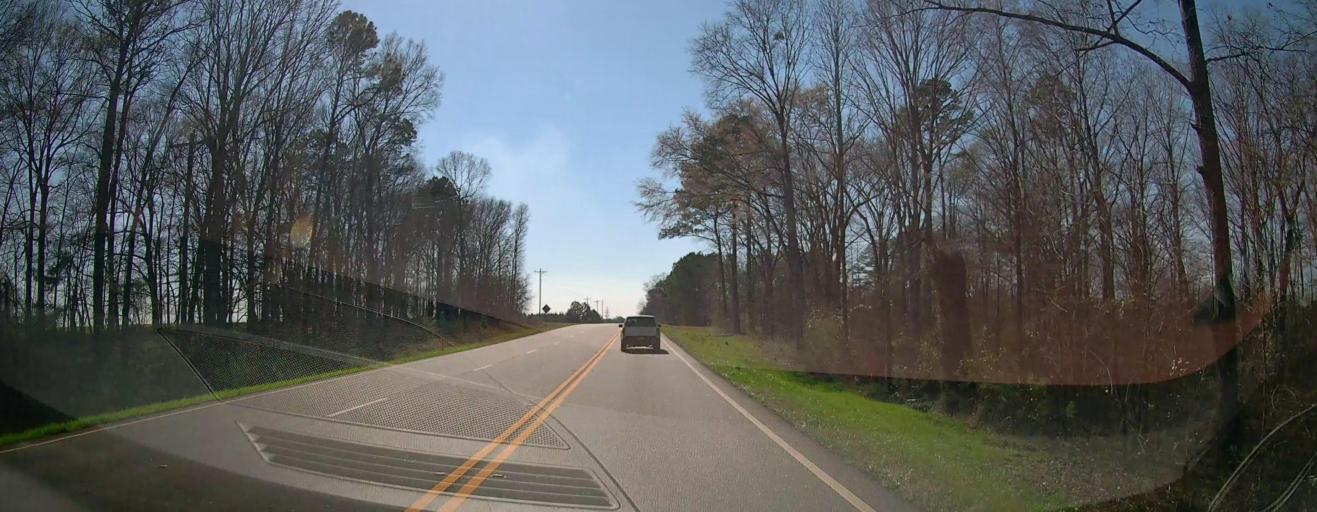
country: US
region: Georgia
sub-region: Macon County
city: Marshallville
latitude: 32.3315
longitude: -83.8657
